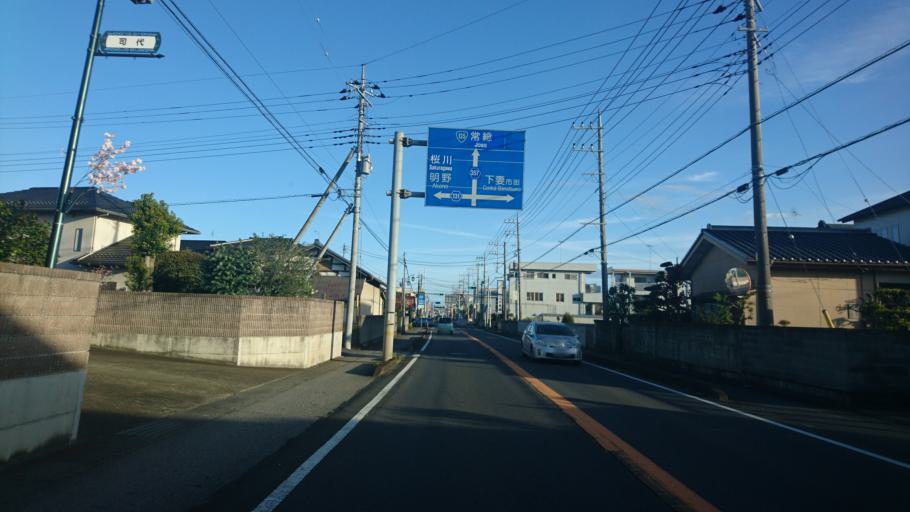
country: JP
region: Ibaraki
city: Ishige
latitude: 36.1874
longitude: 139.9654
